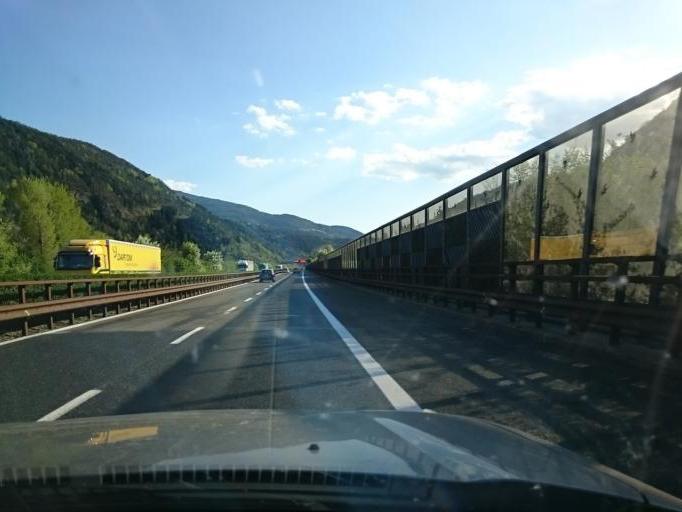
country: IT
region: Trentino-Alto Adige
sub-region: Bolzano
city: Velturno
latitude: 46.6733
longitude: 11.6189
